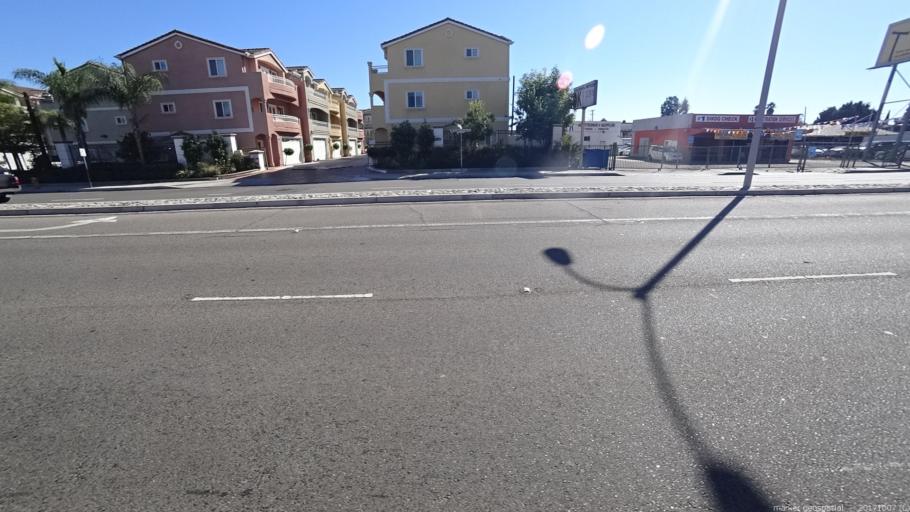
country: US
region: California
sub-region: Orange County
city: Westminster
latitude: 33.7739
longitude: -117.9879
